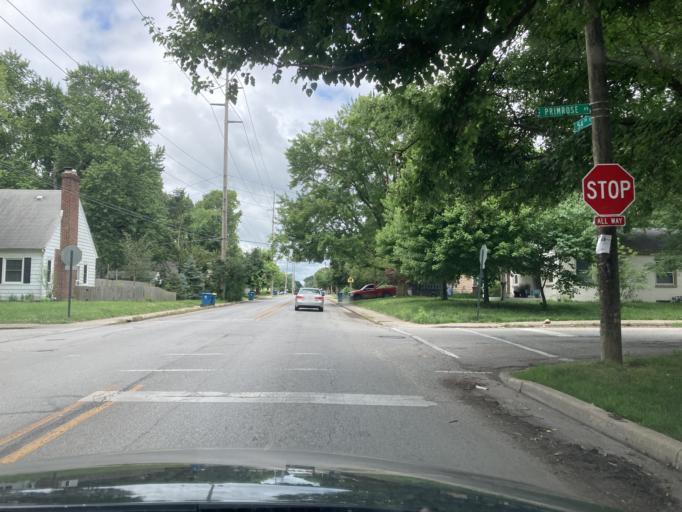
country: US
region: Indiana
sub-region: Marion County
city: Broad Ripple
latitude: 39.8513
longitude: -86.1324
